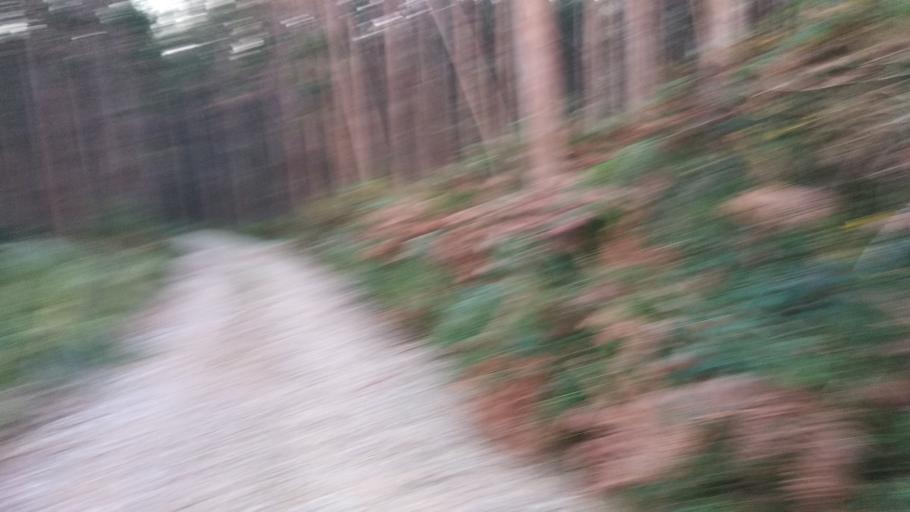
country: ES
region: Cantabria
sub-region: Provincia de Cantabria
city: Entrambasaguas
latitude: 43.3287
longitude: -3.6835
